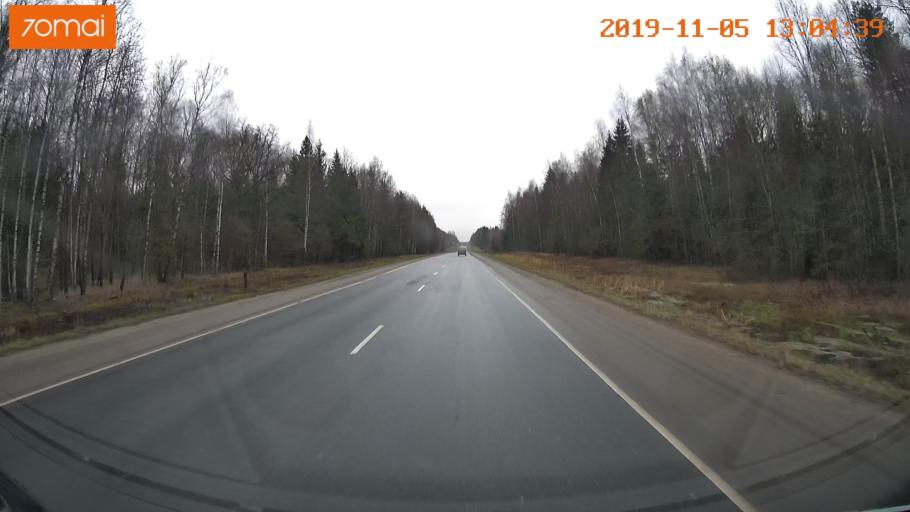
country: RU
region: Ivanovo
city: Kitovo
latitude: 56.8876
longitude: 41.2259
